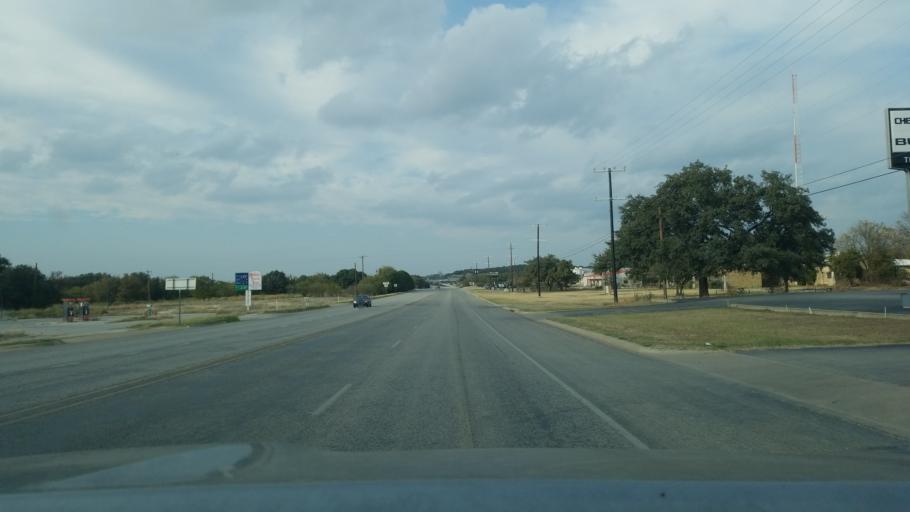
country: US
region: Texas
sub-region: Mills County
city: Goldthwaite
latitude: 31.4710
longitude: -98.5683
